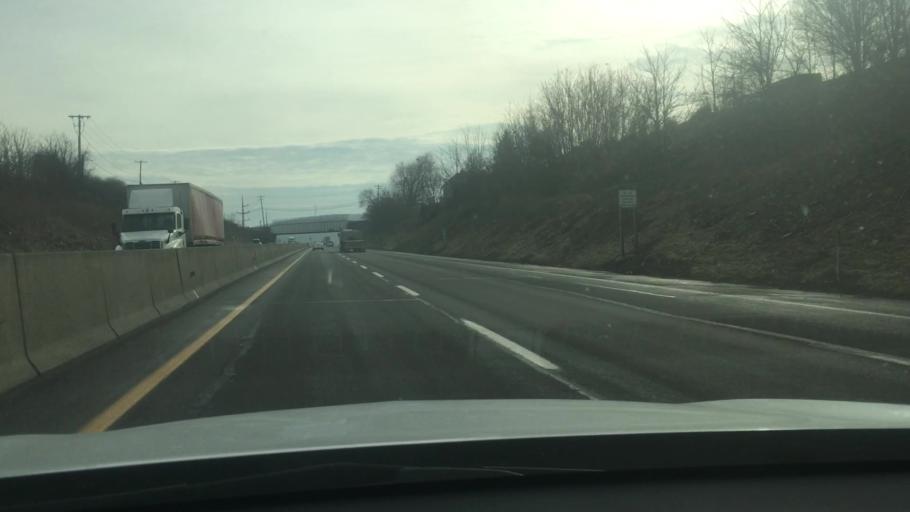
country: US
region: Pennsylvania
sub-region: Chester County
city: Elverson
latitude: 40.1573
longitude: -75.8756
